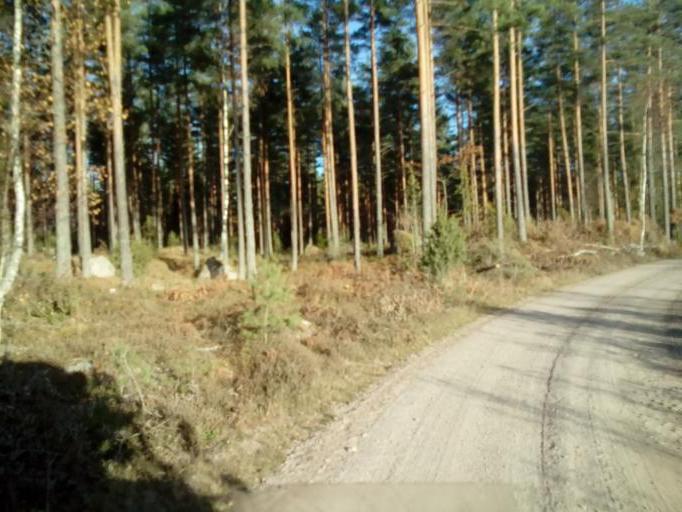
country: SE
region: Kalmar
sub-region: Vimmerby Kommun
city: Vimmerby
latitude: 57.6850
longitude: 15.9211
